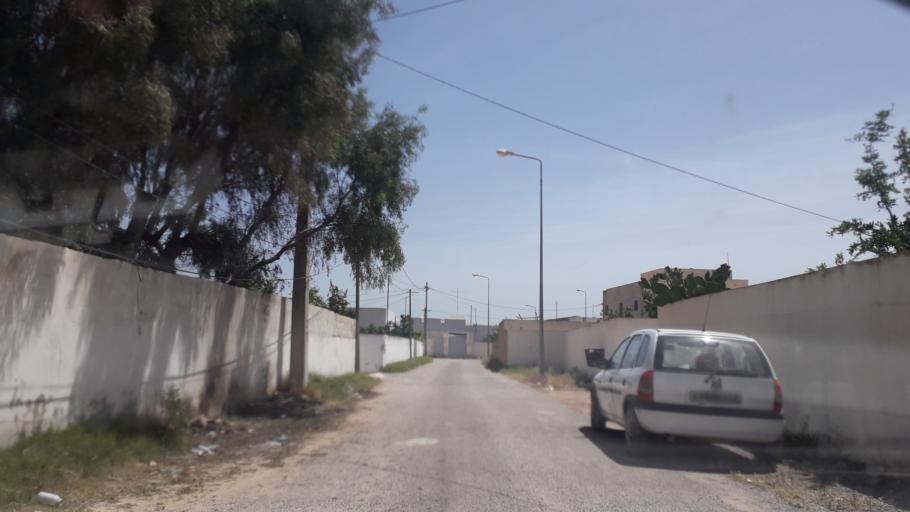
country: TN
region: Safaqis
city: Al Qarmadah
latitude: 34.8041
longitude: 10.7619
